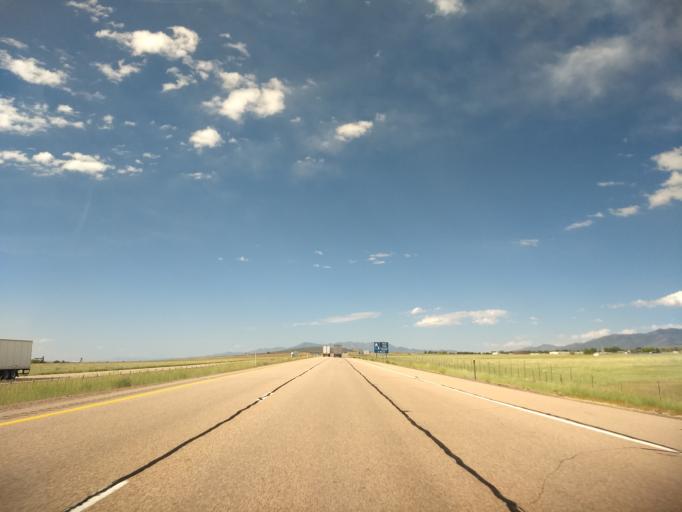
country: US
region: Utah
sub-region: Millard County
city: Fillmore
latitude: 38.9551
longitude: -112.3471
